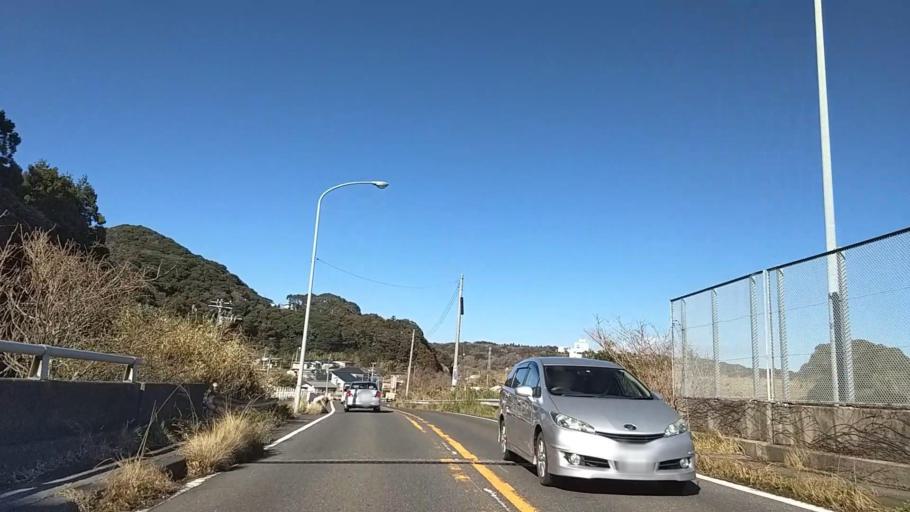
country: JP
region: Chiba
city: Kawaguchi
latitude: 35.0793
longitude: 140.0966
